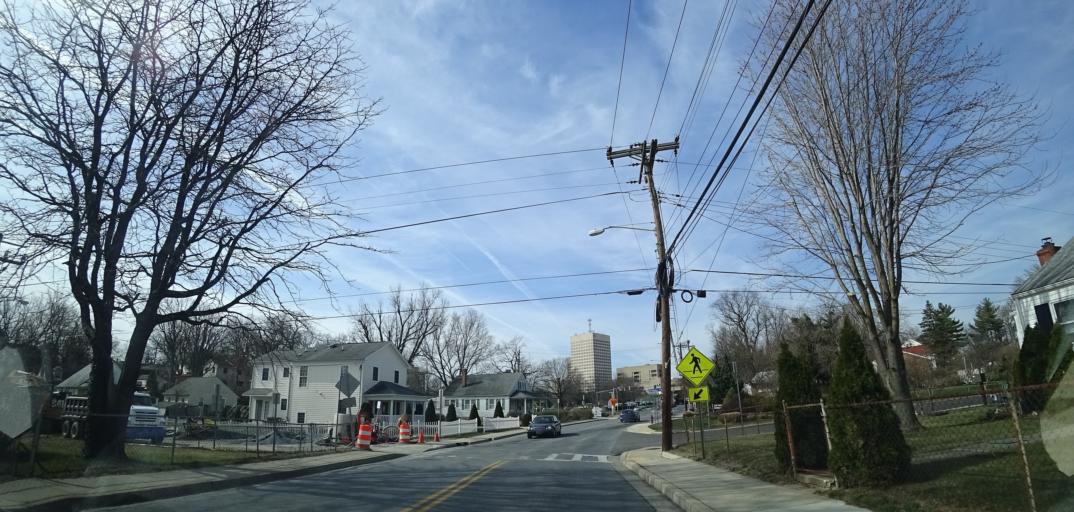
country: US
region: Maryland
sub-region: Montgomery County
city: Rockville
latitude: 39.0866
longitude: -77.1440
